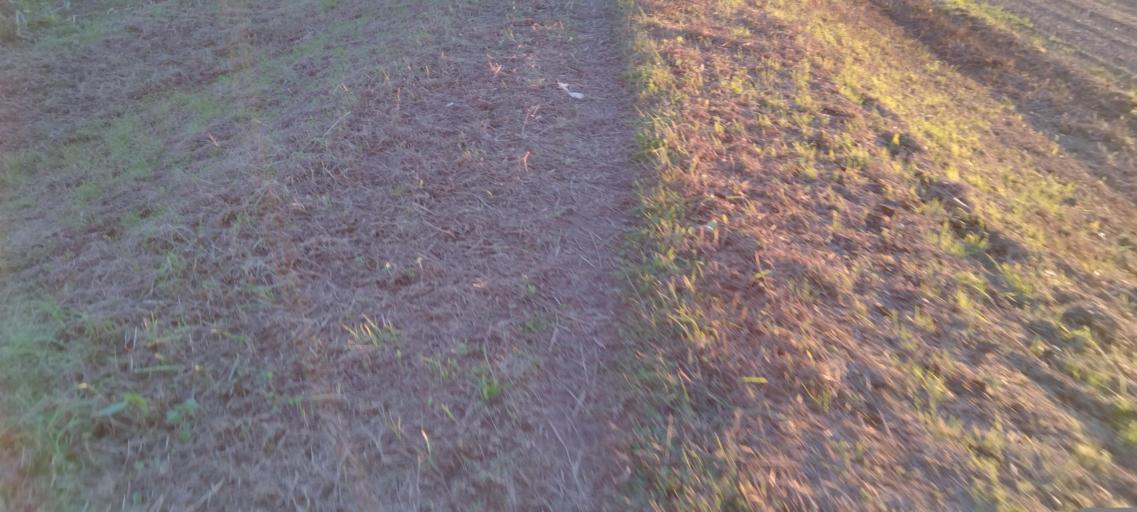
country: IT
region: Veneto
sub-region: Provincia di Vicenza
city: Torri di Quartesolo
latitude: 45.5163
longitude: 11.6113
